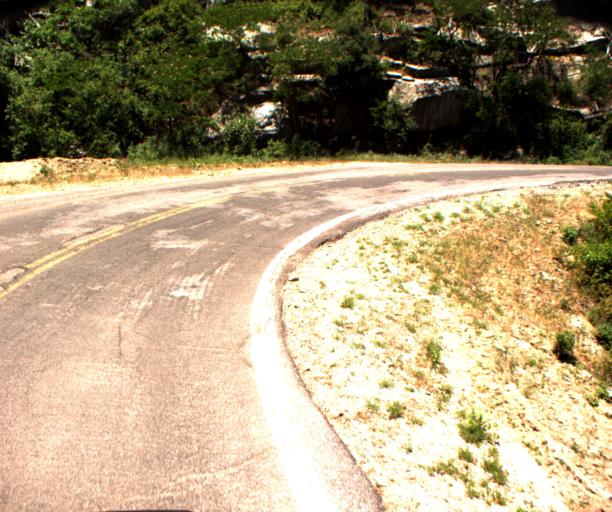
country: US
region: Arizona
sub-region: Graham County
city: Swift Trail Junction
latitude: 32.6280
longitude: -109.8232
